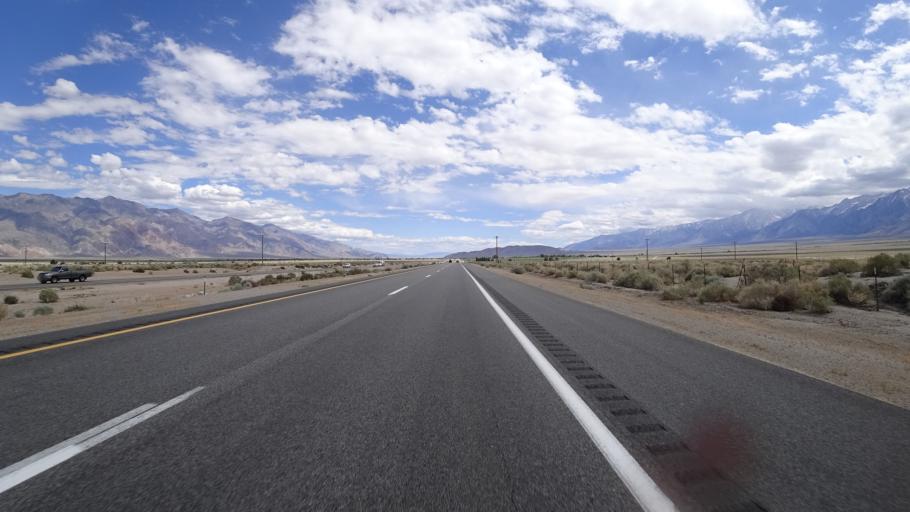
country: US
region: California
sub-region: Inyo County
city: Lone Pine
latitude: 36.7616
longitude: -118.1673
